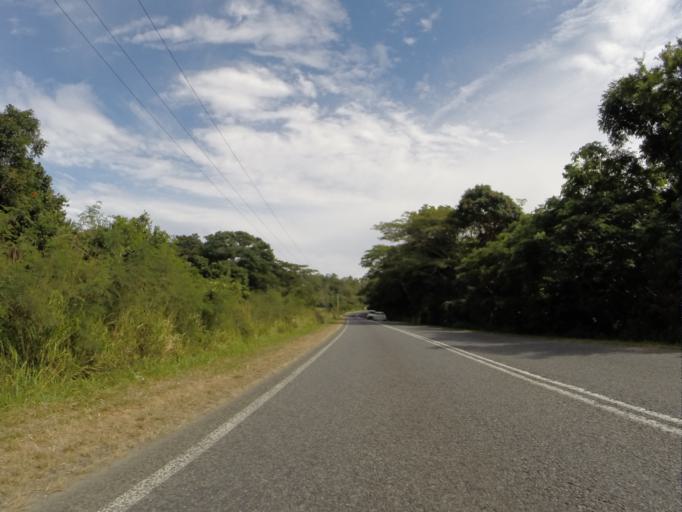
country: FJ
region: Western
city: Nadi
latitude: -18.1227
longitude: 177.4148
